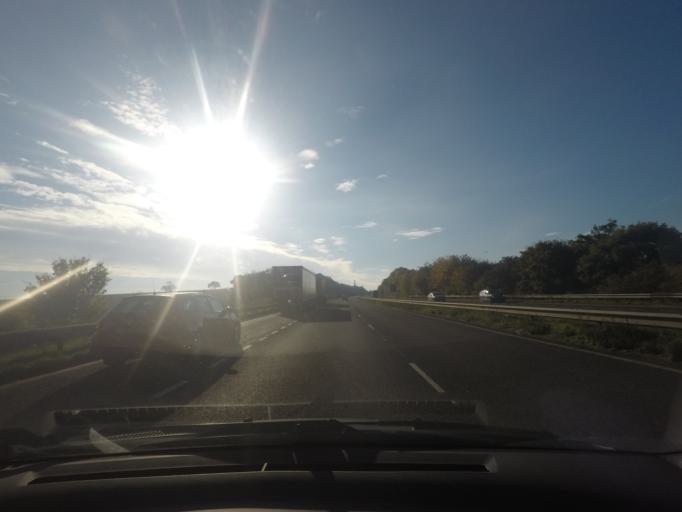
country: GB
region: England
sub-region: North Lincolnshire
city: Barton upon Humber
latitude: 53.6708
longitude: -0.4509
